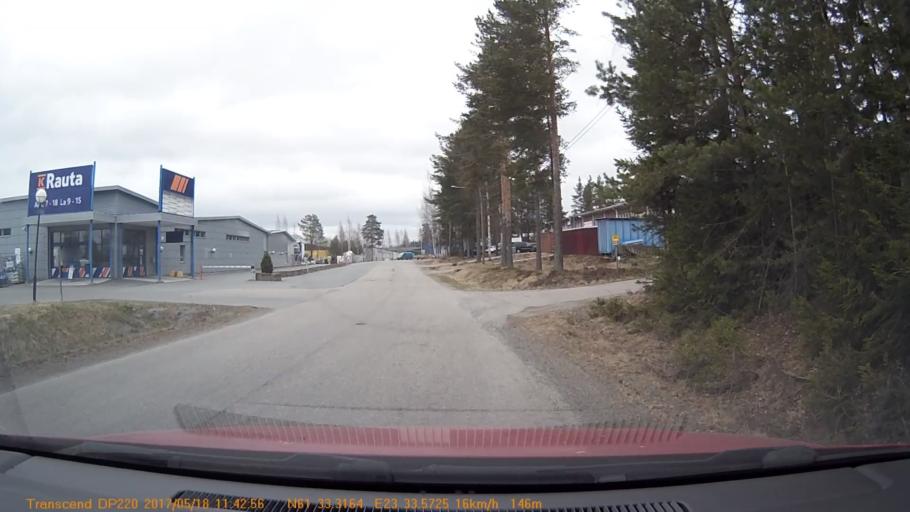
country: FI
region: Pirkanmaa
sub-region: Tampere
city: Yloejaervi
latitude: 61.5552
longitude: 23.5594
